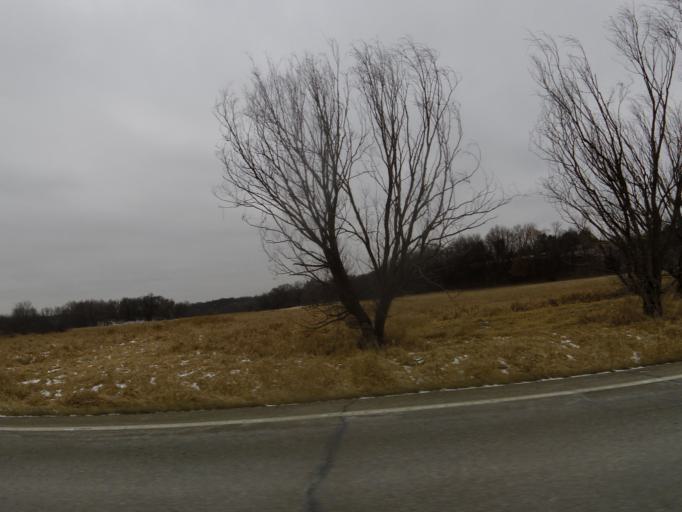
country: US
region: Minnesota
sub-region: Hennepin County
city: Independence
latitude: 45.0189
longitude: -93.7273
